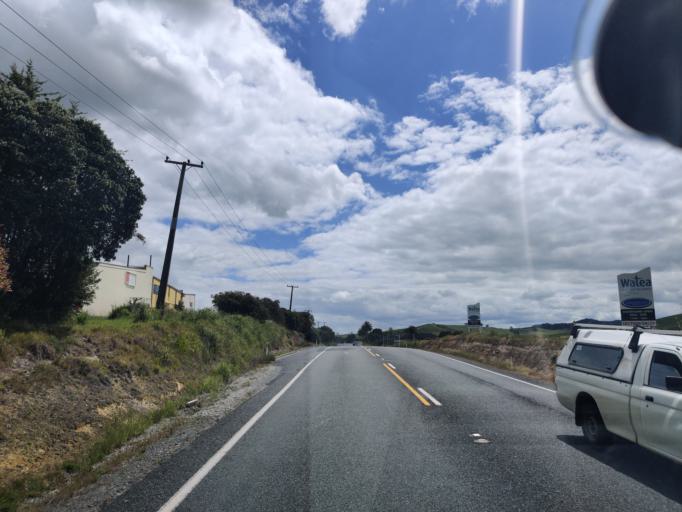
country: NZ
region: Northland
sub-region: Far North District
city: Paihia
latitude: -35.2809
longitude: 174.0476
